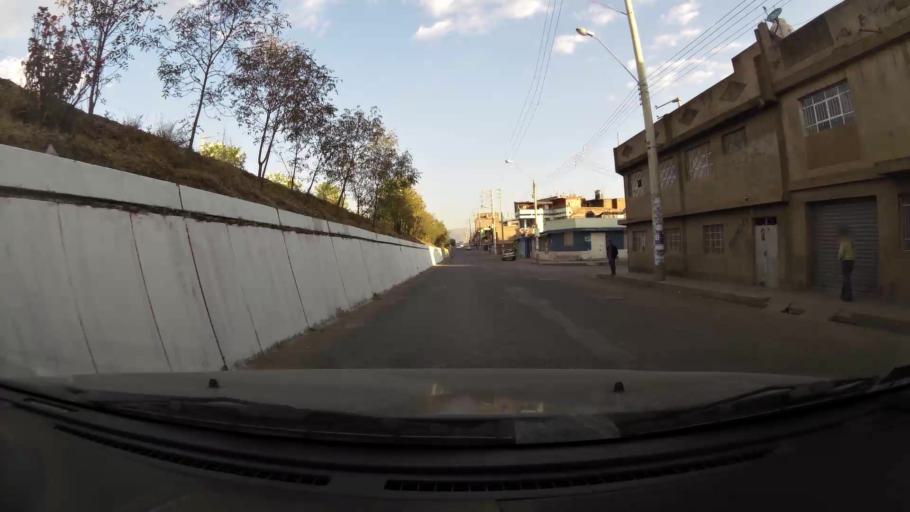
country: PE
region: Junin
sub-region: Provincia de Huancayo
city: El Tambo
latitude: -12.0526
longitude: -75.2142
